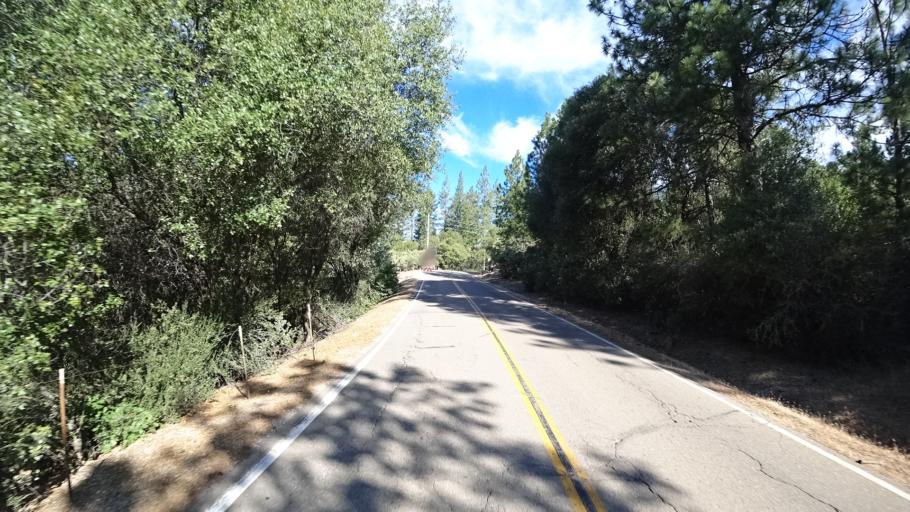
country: US
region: California
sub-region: Amador County
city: Pioneer
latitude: 38.3742
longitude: -120.5091
